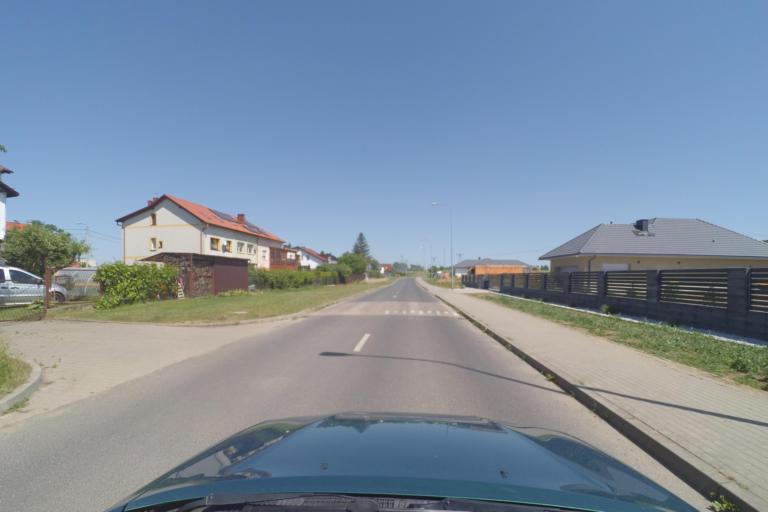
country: PL
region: Lower Silesian Voivodeship
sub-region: Powiat zlotoryjski
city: Zlotoryja
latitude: 51.1136
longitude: 15.9067
